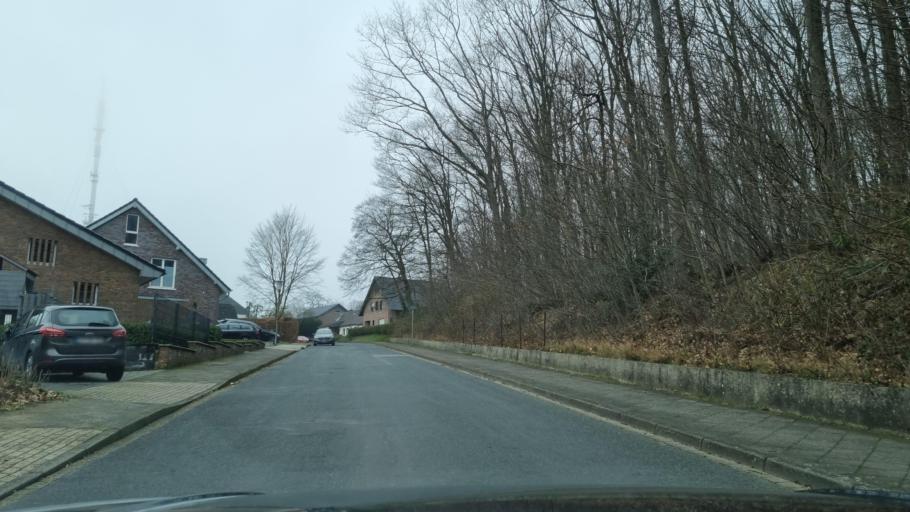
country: DE
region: North Rhine-Westphalia
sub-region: Regierungsbezirk Dusseldorf
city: Kleve
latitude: 51.7875
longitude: 6.1159
